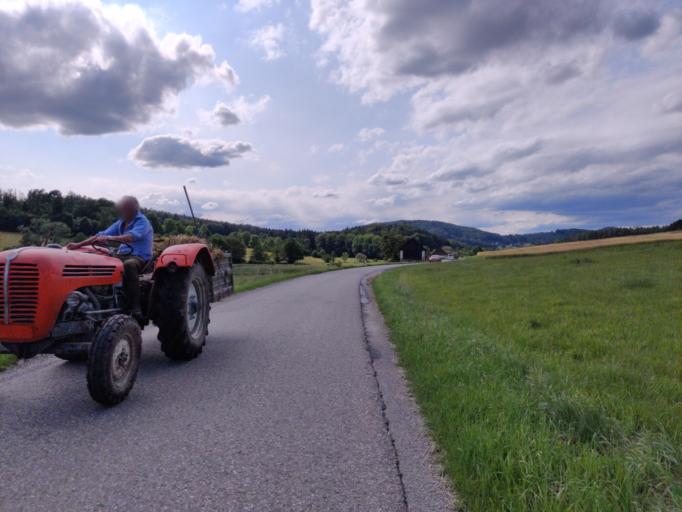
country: AT
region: Styria
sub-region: Politischer Bezirk Graz-Umgebung
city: Thal
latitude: 47.0587
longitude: 15.3529
